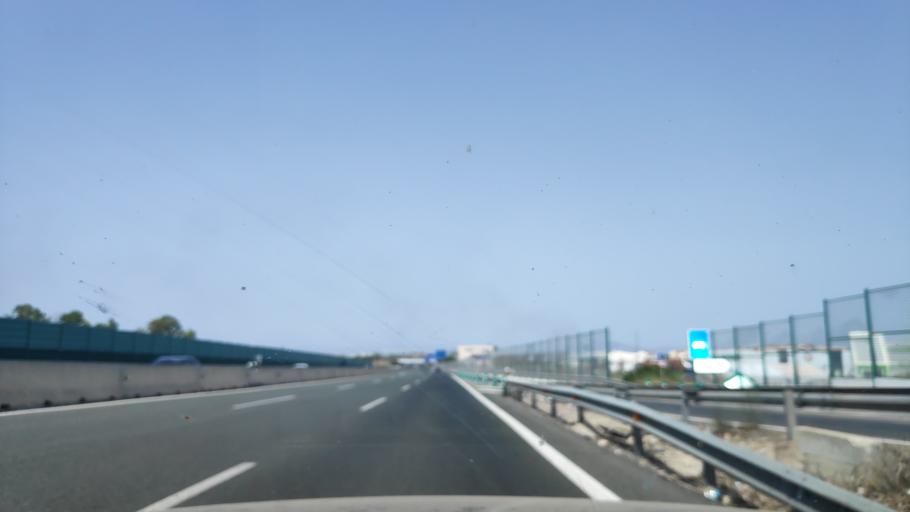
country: ES
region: Murcia
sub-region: Murcia
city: Murcia
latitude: 37.9378
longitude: -1.1520
